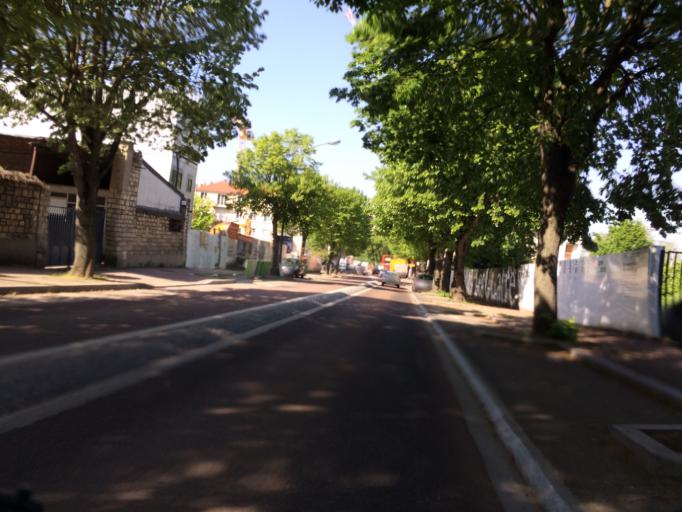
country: FR
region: Ile-de-France
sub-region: Departement des Hauts-de-Seine
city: Sceaux
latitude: 48.7807
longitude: 2.2808
